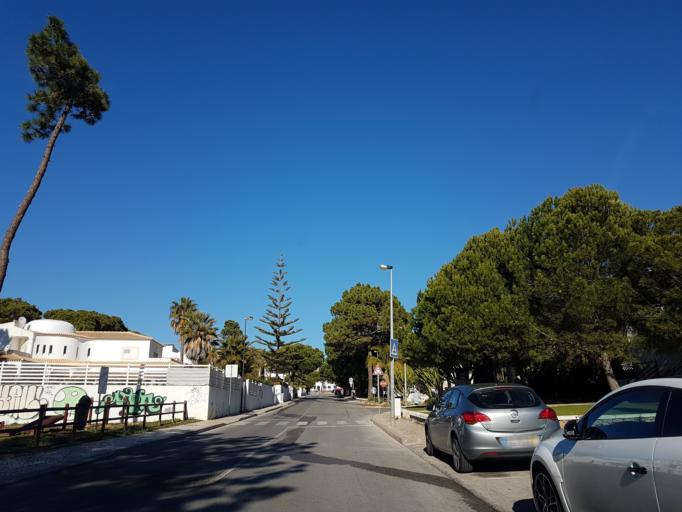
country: PT
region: Faro
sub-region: Loule
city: Boliqueime
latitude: 37.0906
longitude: -8.1678
